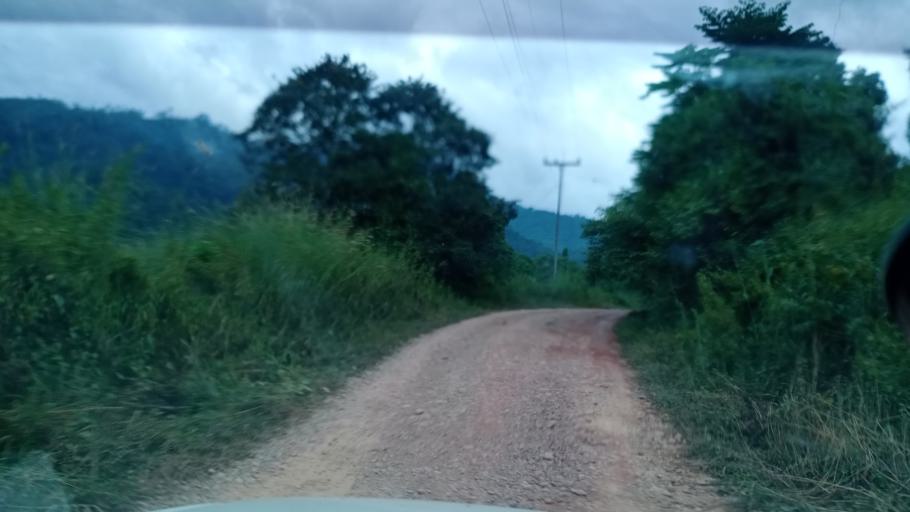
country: TH
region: Changwat Bueng Kan
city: Pak Khat
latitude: 18.7224
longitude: 103.2351
